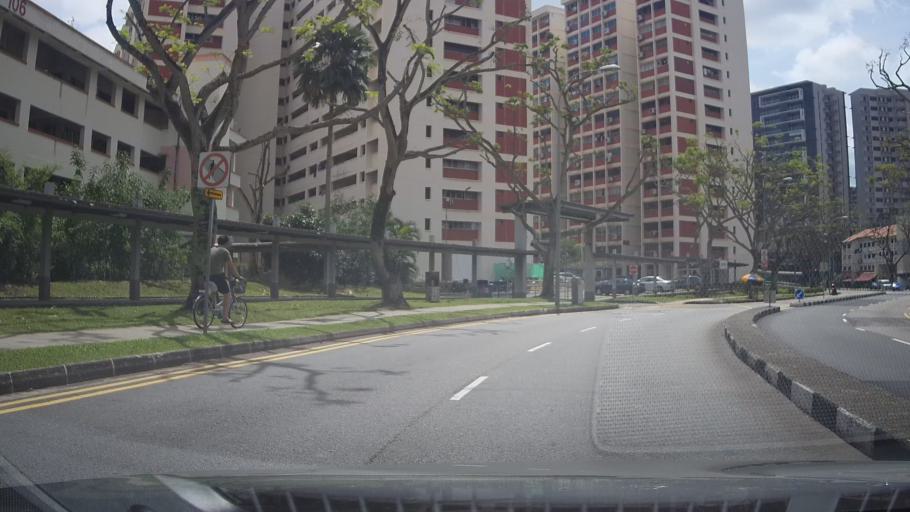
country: SG
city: Singapore
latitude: 1.3341
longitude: 103.8678
